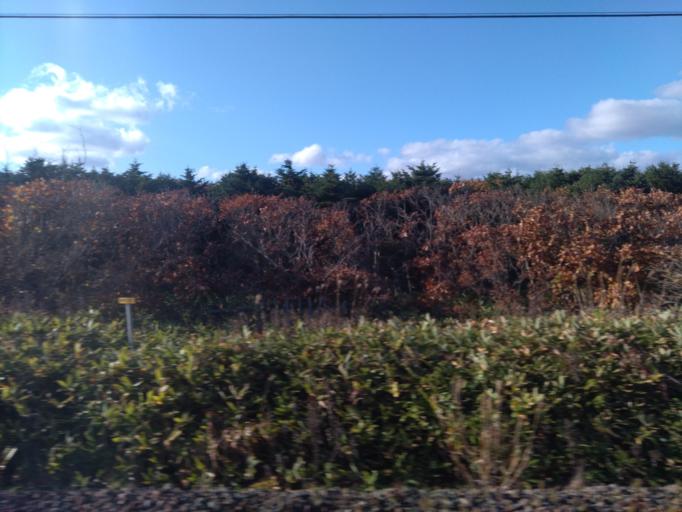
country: JP
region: Hokkaido
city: Niseko Town
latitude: 42.5502
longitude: 140.4174
